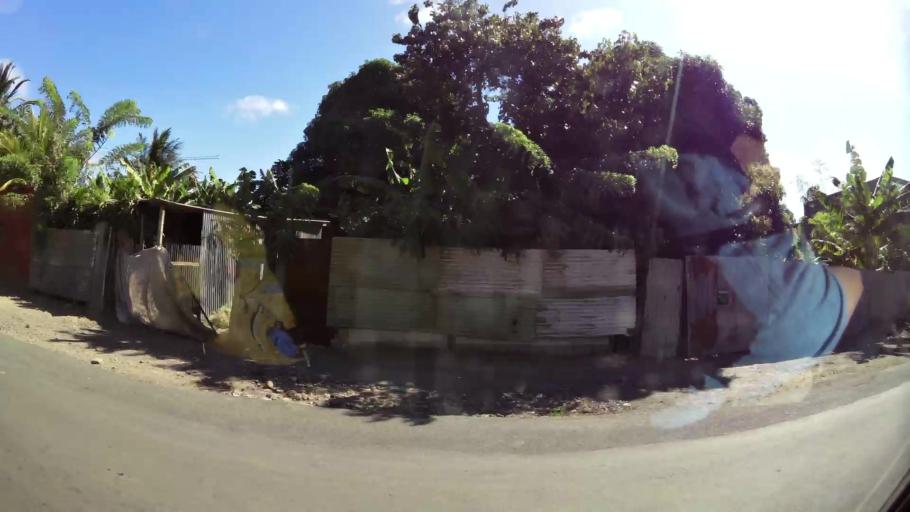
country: YT
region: Pamandzi
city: Pamandzi
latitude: -12.7792
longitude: 45.2812
